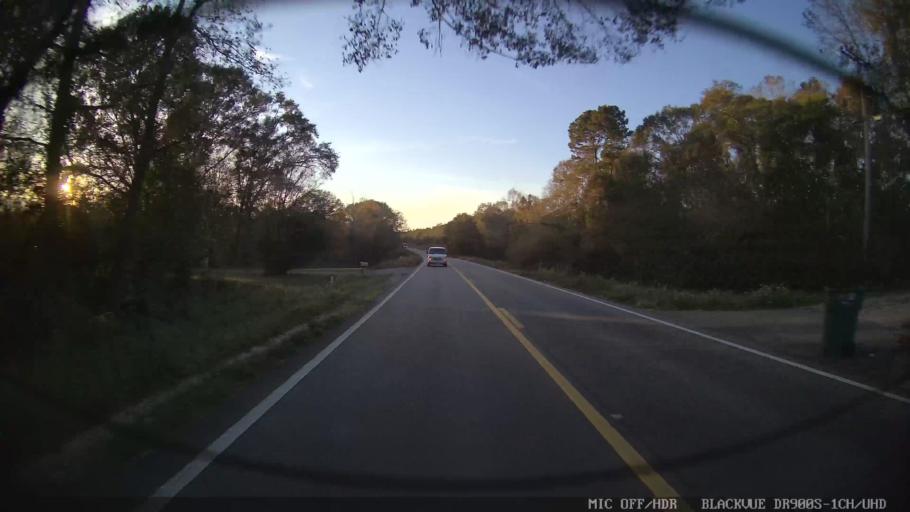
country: US
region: Mississippi
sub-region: Stone County
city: Wiggins
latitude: 30.9885
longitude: -89.2623
